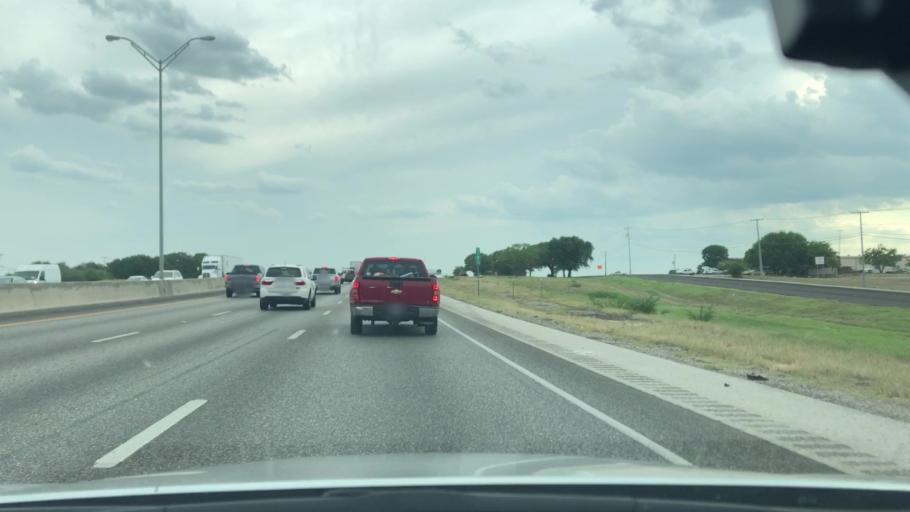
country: US
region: Texas
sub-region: Guadalupe County
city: Northcliff
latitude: 29.6353
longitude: -98.2217
